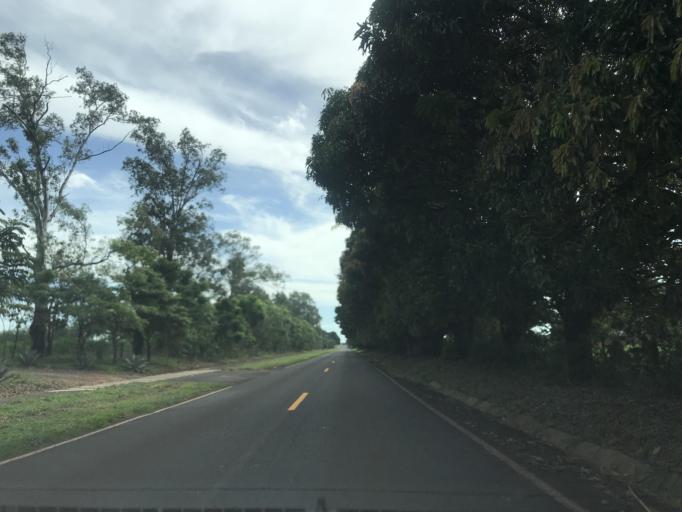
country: BR
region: Parana
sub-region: Terra Rica
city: Terra Rica
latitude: -22.7620
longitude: -52.6357
